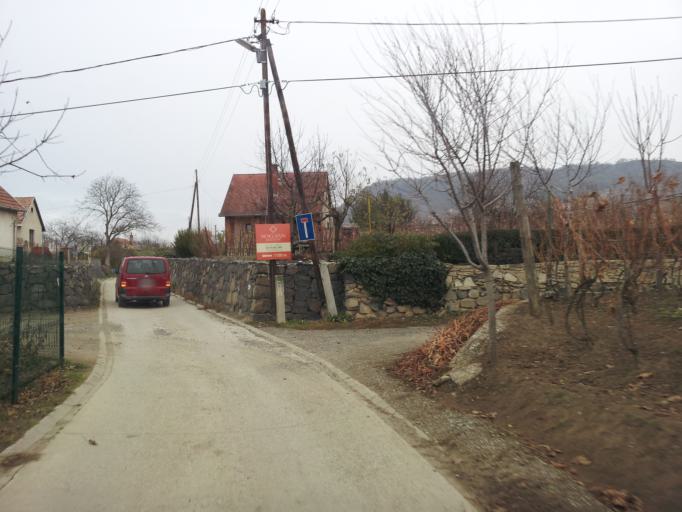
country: HU
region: Veszprem
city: Devecser
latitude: 47.1323
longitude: 17.3709
